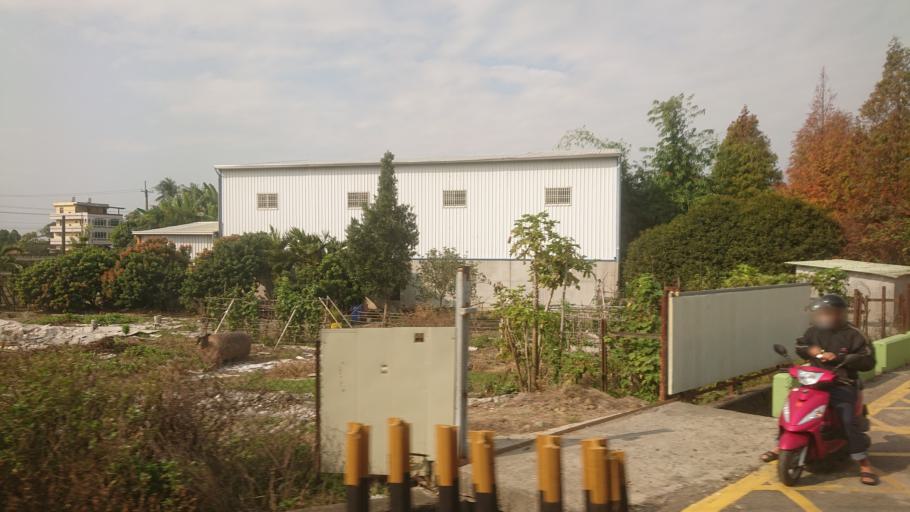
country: TW
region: Taiwan
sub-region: Nantou
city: Nantou
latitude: 23.9262
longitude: 120.5722
